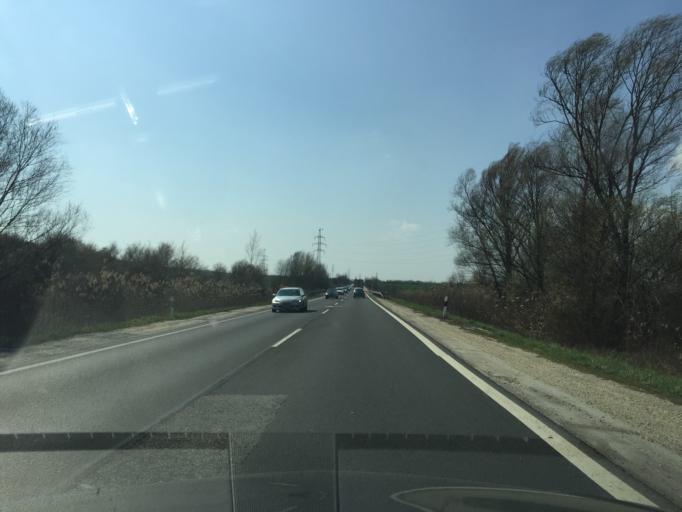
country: HU
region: Pest
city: Szod
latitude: 47.7605
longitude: 19.1809
